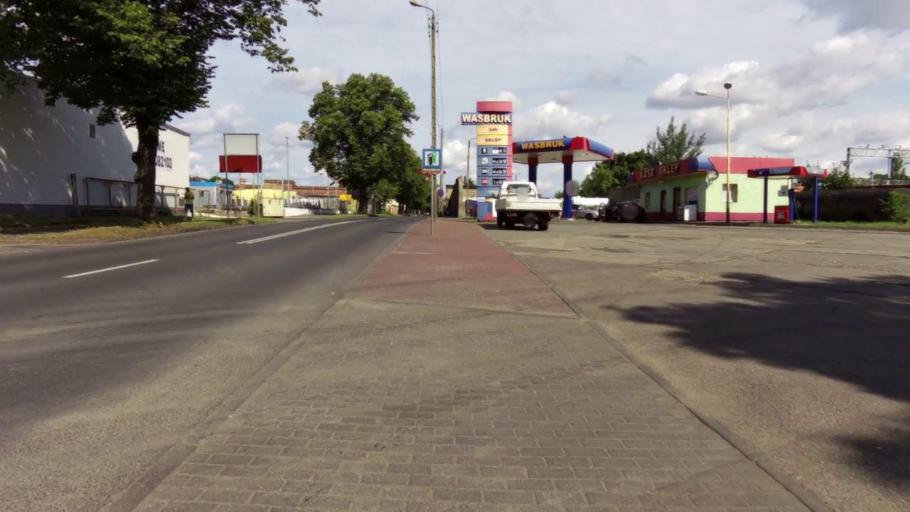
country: PL
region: West Pomeranian Voivodeship
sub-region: Powiat stargardzki
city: Stargard Szczecinski
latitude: 53.3340
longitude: 15.0342
